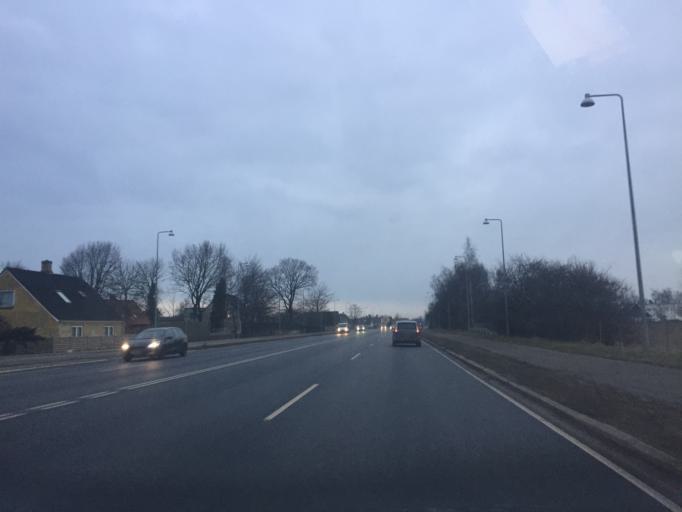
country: DK
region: Zealand
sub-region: Koge Kommune
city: Koge
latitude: 55.4945
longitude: 12.1925
